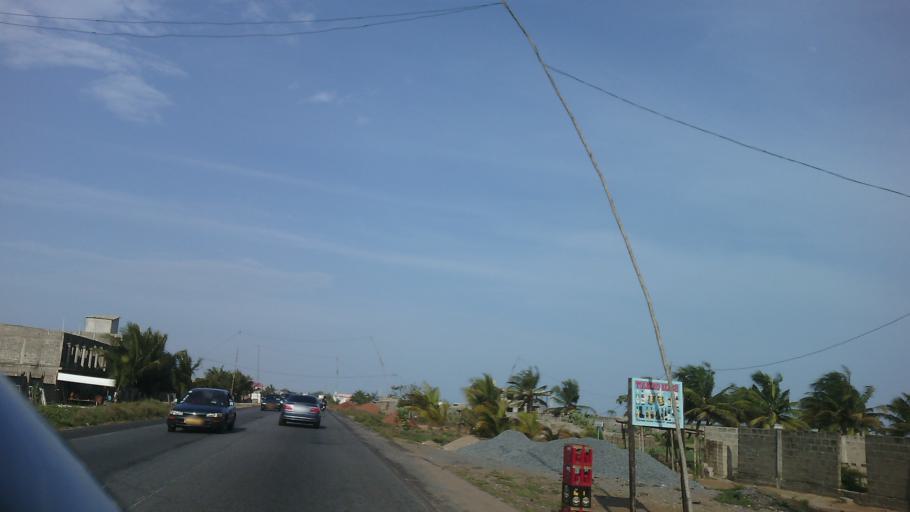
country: TG
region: Maritime
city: Lome
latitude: 6.1790
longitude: 1.3810
